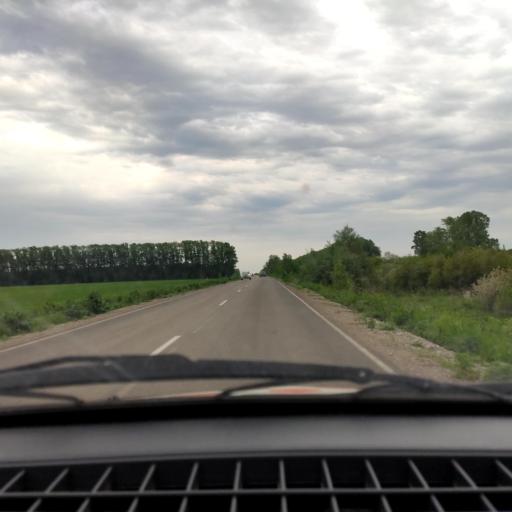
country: RU
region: Bashkortostan
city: Avdon
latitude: 54.5369
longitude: 55.7631
